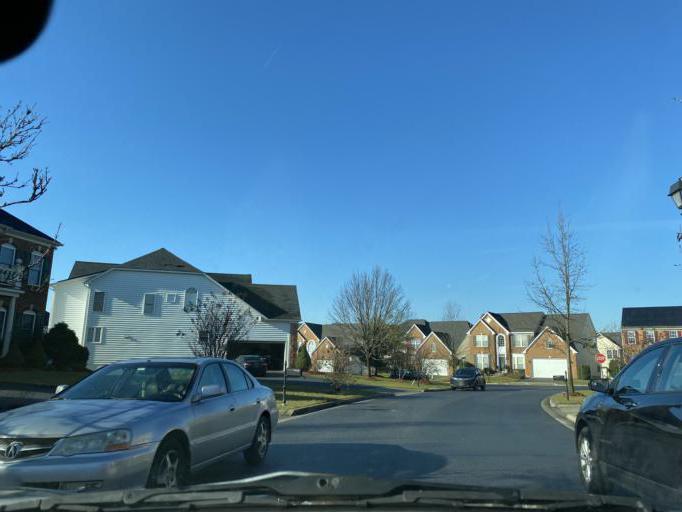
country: US
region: Maryland
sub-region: Prince George's County
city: South Laurel
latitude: 39.0834
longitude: -76.8725
